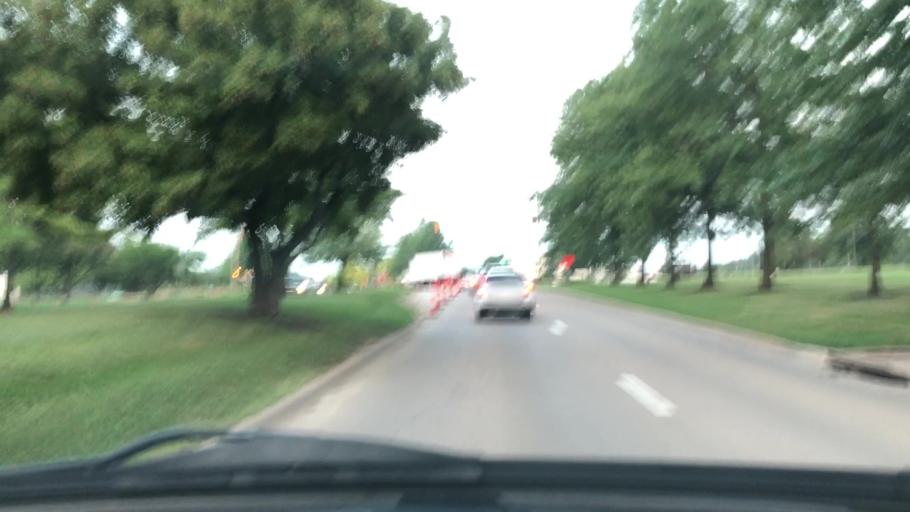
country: US
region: Iowa
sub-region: Johnson County
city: Coralville
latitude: 41.7084
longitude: -91.6061
